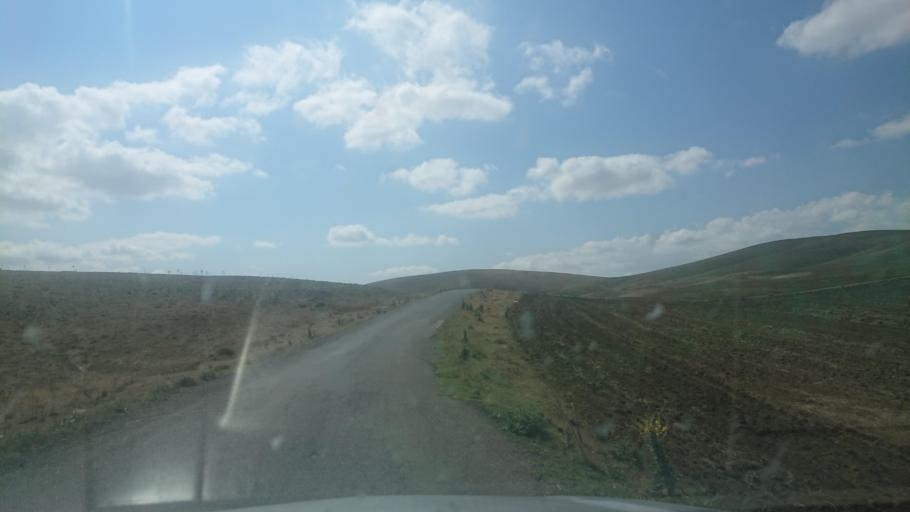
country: TR
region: Aksaray
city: Sariyahsi
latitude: 39.0052
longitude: 33.9592
